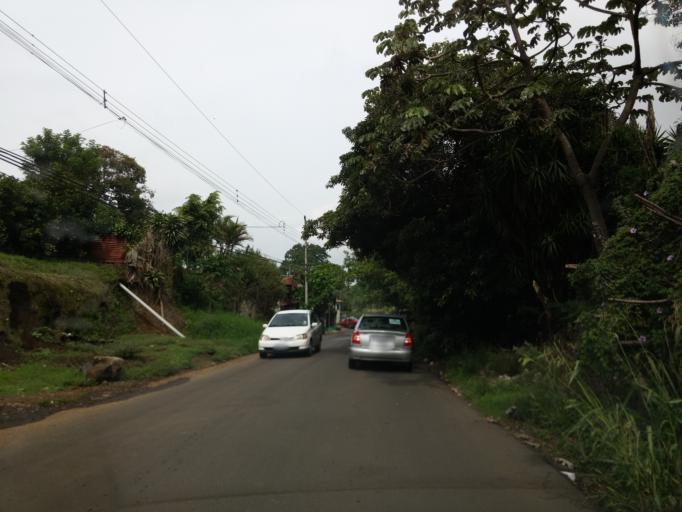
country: CR
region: Heredia
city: Llorente
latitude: 10.0150
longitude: -84.1698
